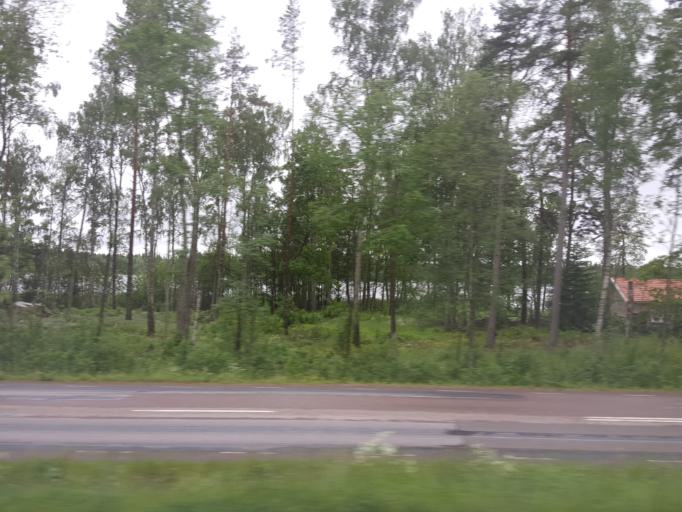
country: SE
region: Vaestmanland
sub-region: Sala Kommun
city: Sala
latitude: 59.9408
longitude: 16.5554
